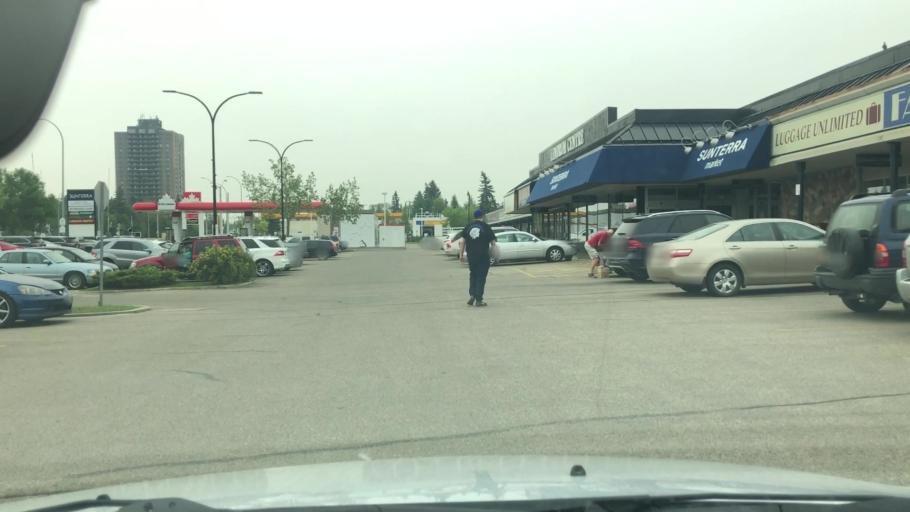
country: CA
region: Alberta
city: Edmonton
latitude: 53.4954
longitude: -113.5174
